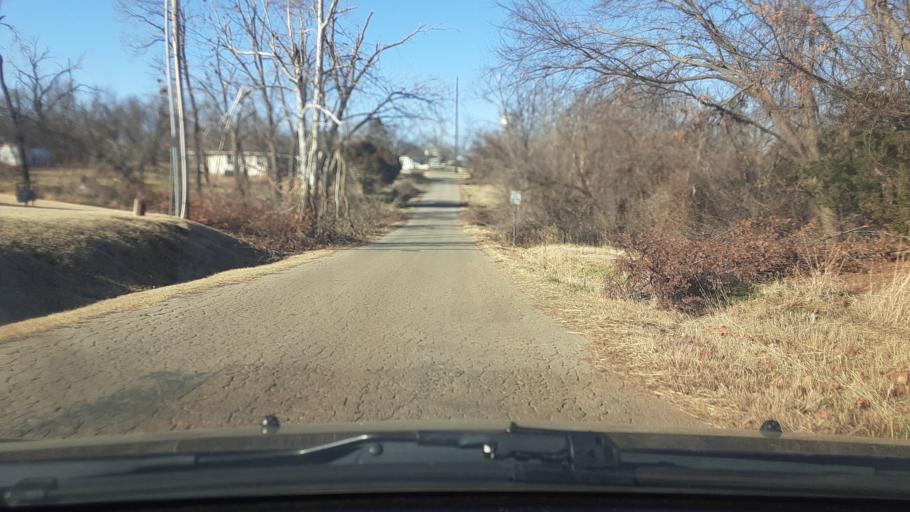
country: US
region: Oklahoma
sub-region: Logan County
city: Guthrie
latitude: 35.8770
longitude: -97.4055
